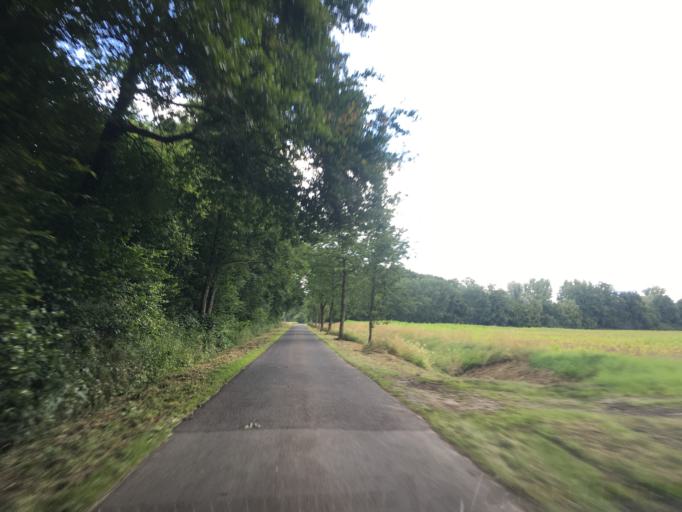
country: DE
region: North Rhine-Westphalia
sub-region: Regierungsbezirk Munster
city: Muenster
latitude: 52.0212
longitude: 7.5907
